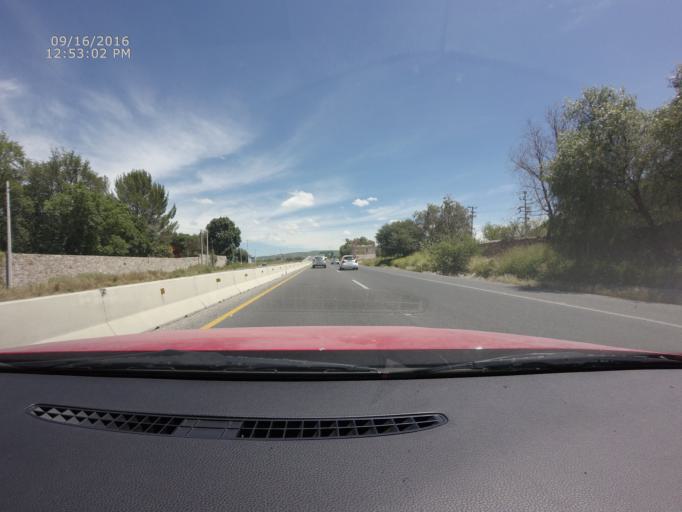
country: MX
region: Queretaro
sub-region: Colon
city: Purisima de Cubos (La Purisima)
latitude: 20.6217
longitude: -100.1338
